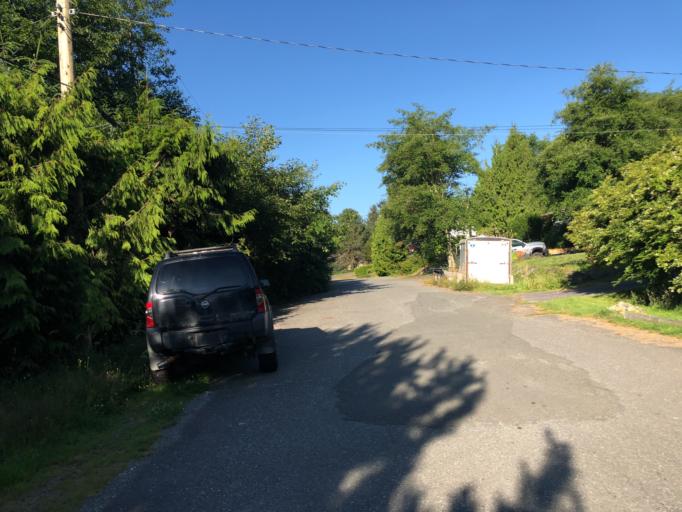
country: CA
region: British Columbia
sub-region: Regional District of Alberni-Clayoquot
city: Ucluelet
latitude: 48.9694
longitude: -125.5875
